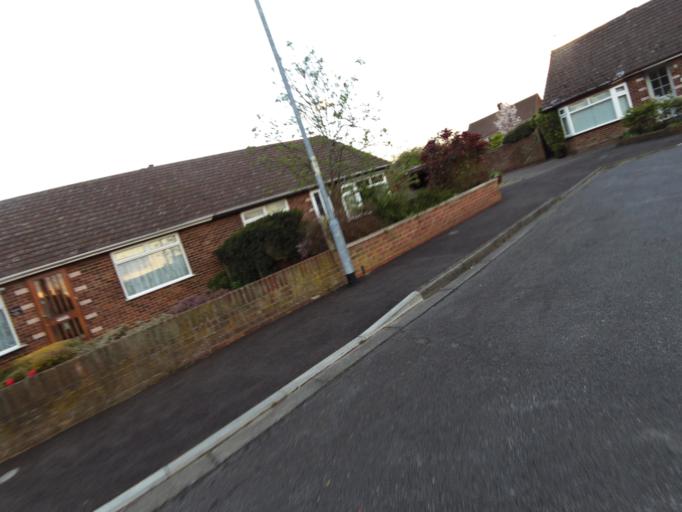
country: GB
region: England
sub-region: Suffolk
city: Ipswich
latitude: 52.0721
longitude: 1.1946
